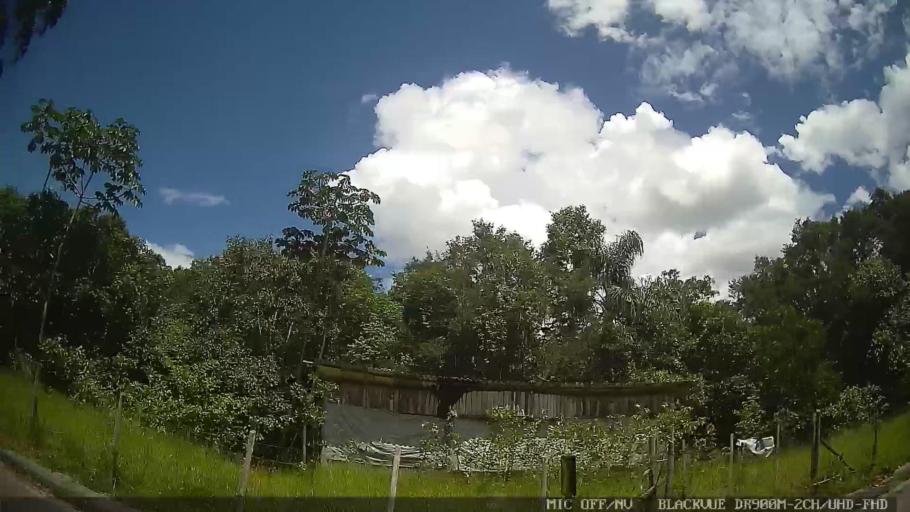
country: BR
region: Sao Paulo
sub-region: Caraguatatuba
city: Caraguatatuba
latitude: -23.5448
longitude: -45.5877
